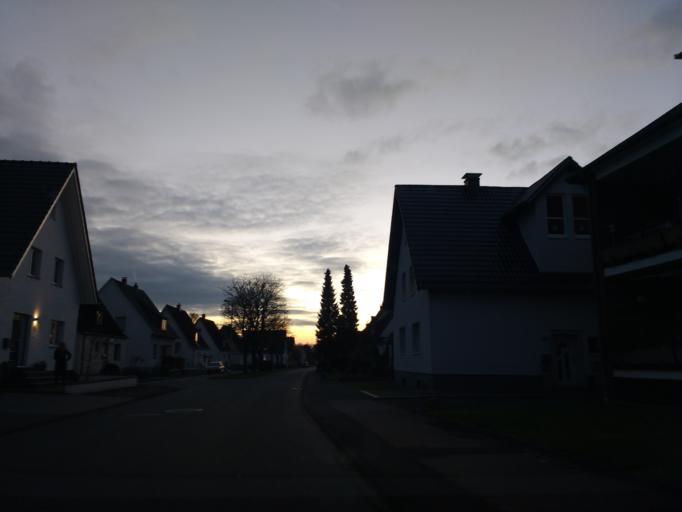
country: DE
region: North Rhine-Westphalia
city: Bad Lippspringe
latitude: 51.7830
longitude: 8.8062
